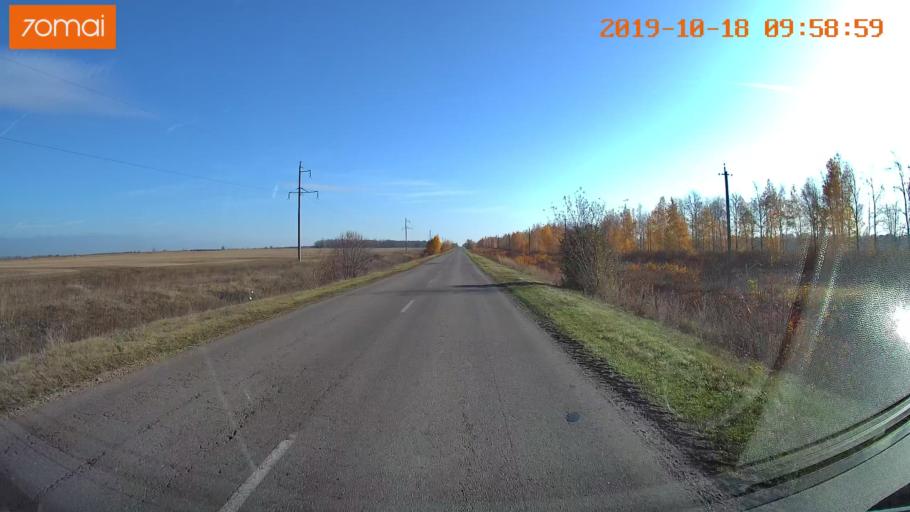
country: RU
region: Tula
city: Kurkino
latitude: 53.3763
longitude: 38.4521
